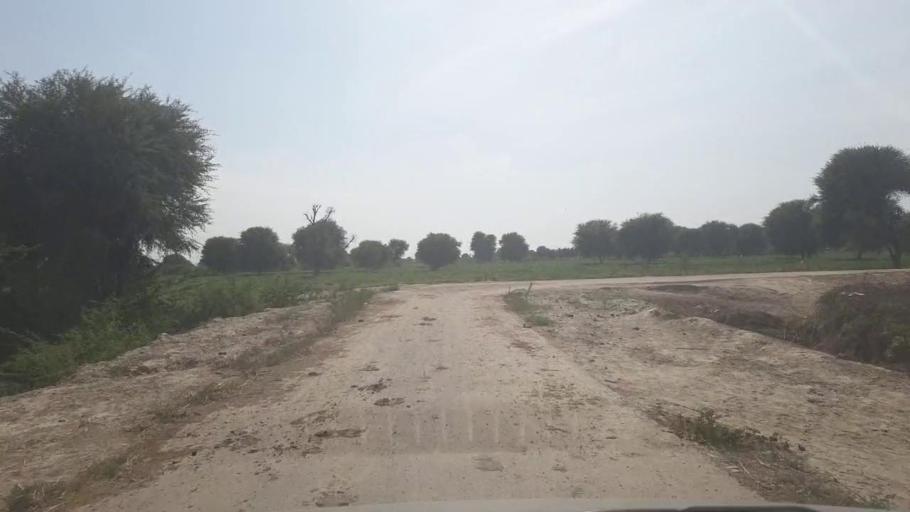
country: PK
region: Sindh
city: Kunri
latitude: 25.1765
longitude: 69.6843
